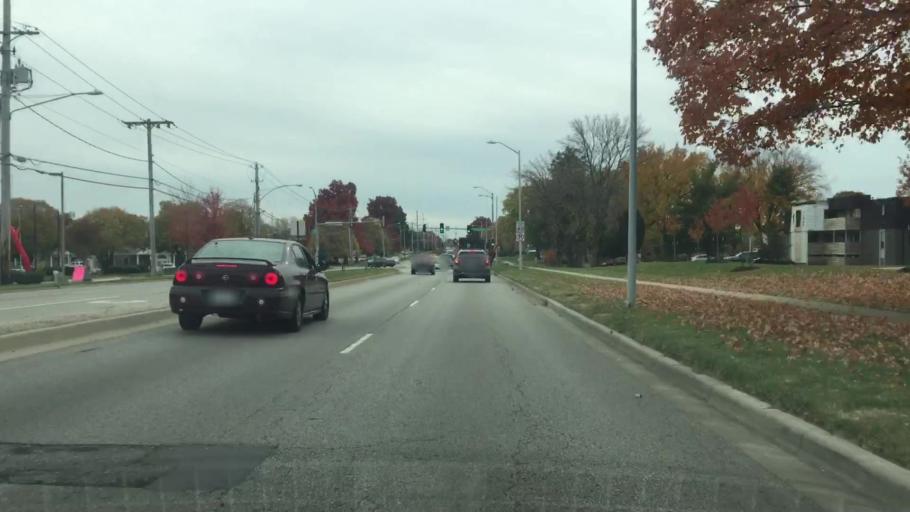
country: US
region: Kansas
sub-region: Johnson County
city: Lenexa
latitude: 38.9890
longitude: -94.7238
